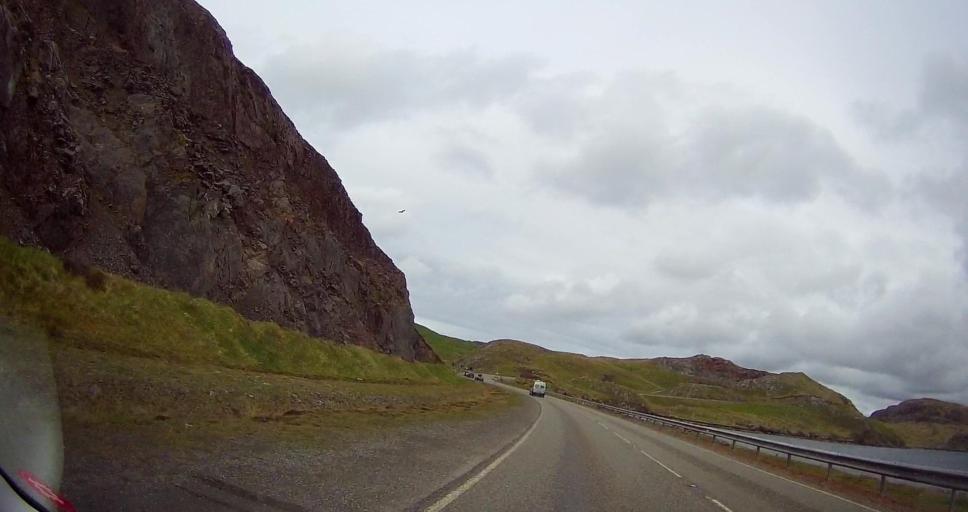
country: GB
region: Scotland
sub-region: Shetland Islands
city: Lerwick
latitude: 60.3960
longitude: -1.3805
